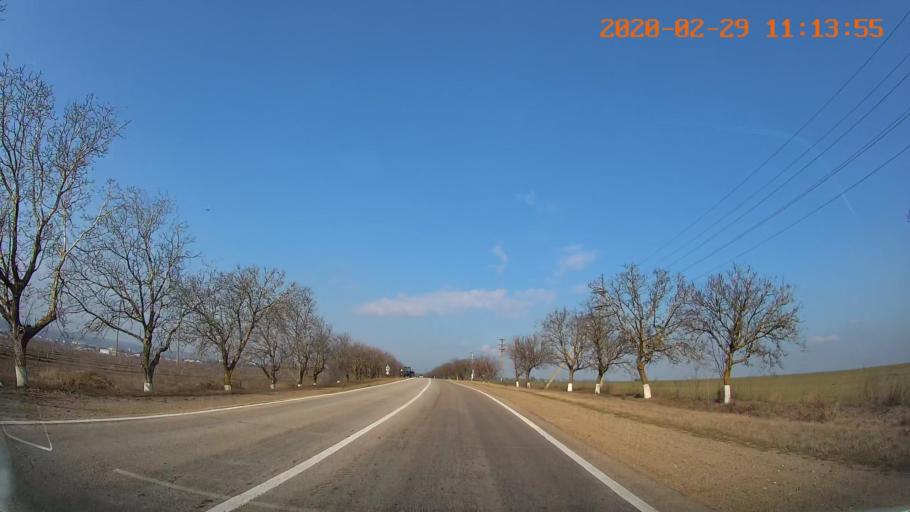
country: MD
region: Telenesti
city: Dubasari
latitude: 47.2770
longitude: 29.1784
